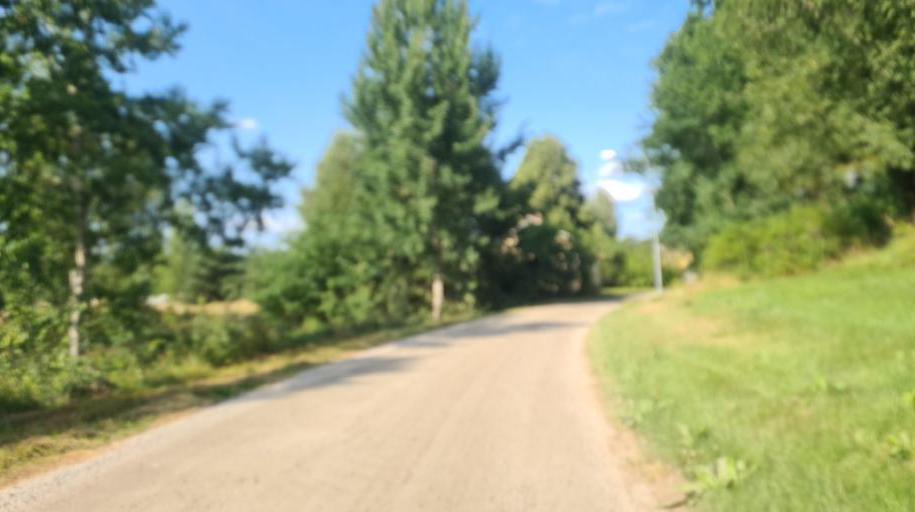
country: SE
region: Kronoberg
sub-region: Ljungby Kommun
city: Ljungby
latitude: 56.7386
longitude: 13.8744
